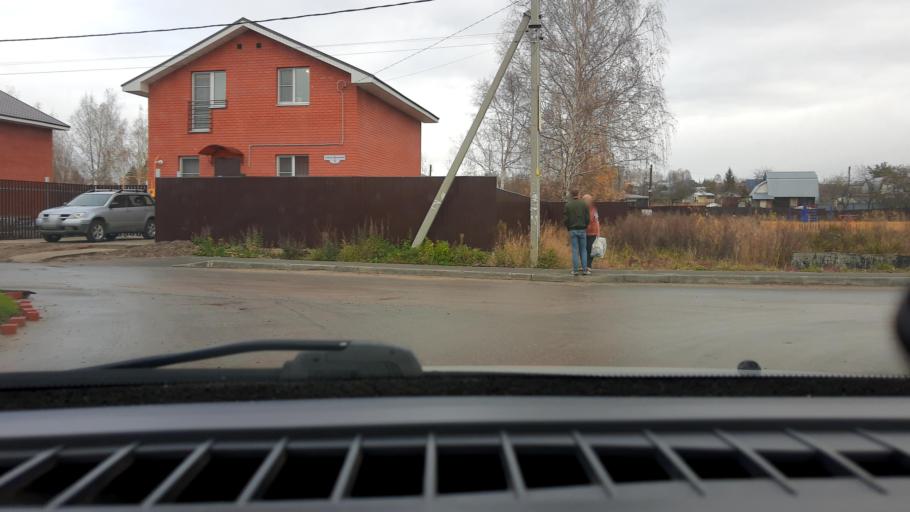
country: RU
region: Nizjnij Novgorod
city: Afonino
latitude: 56.2069
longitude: 44.1237
